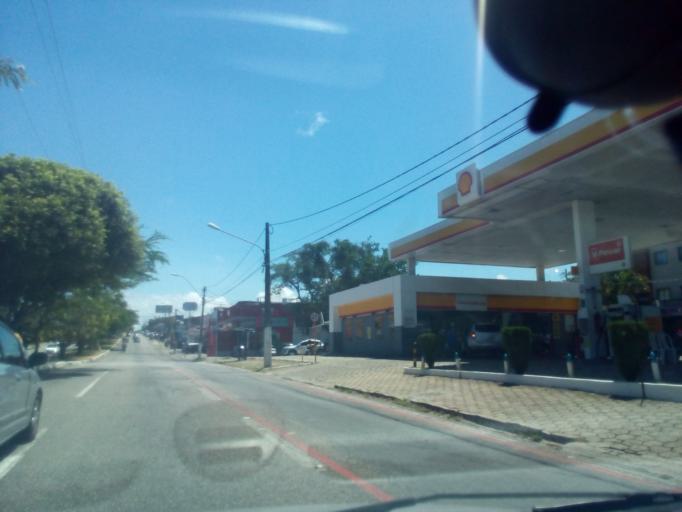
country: BR
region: Rio Grande do Norte
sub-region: Natal
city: Natal
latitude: -5.8320
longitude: -35.2176
